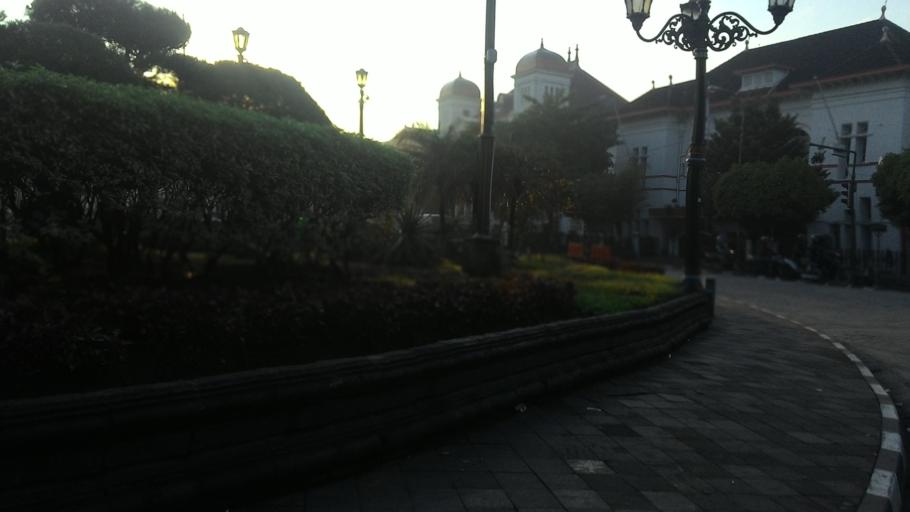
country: ID
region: Daerah Istimewa Yogyakarta
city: Yogyakarta
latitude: -7.8012
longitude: 110.3648
